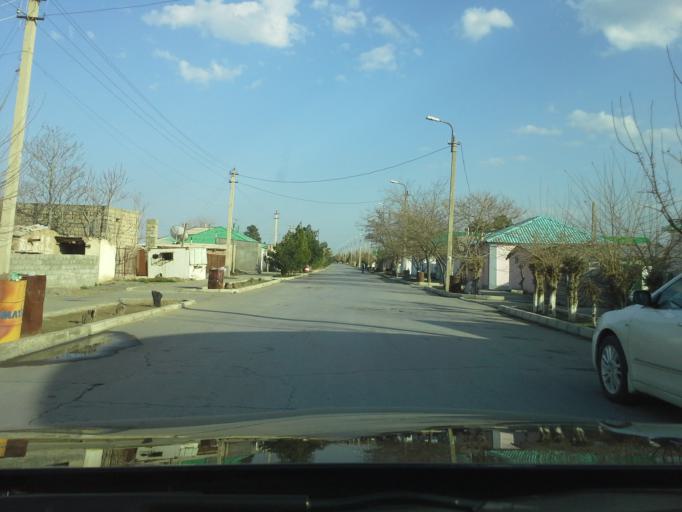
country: TM
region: Ahal
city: Abadan
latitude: 38.0227
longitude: 58.2341
